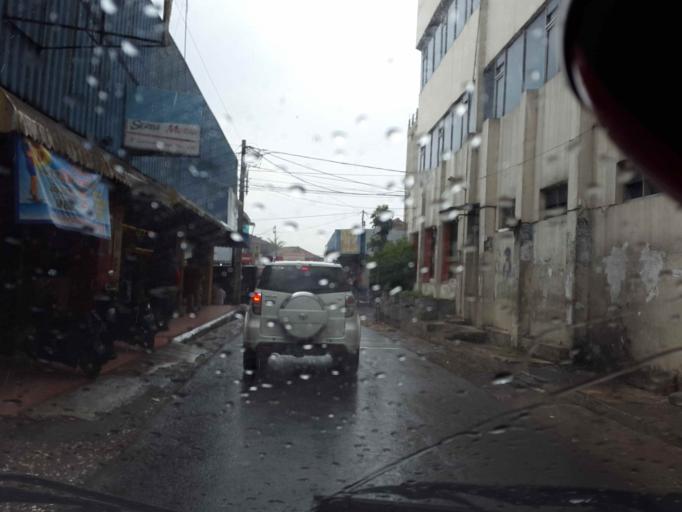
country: ID
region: West Java
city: Cimahi
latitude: -6.8750
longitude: 107.5416
